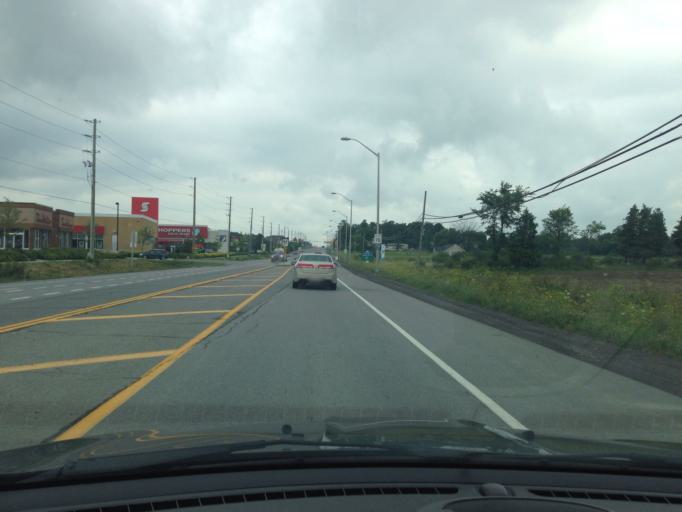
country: CA
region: Ontario
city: Ottawa
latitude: 45.3182
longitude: -75.5923
